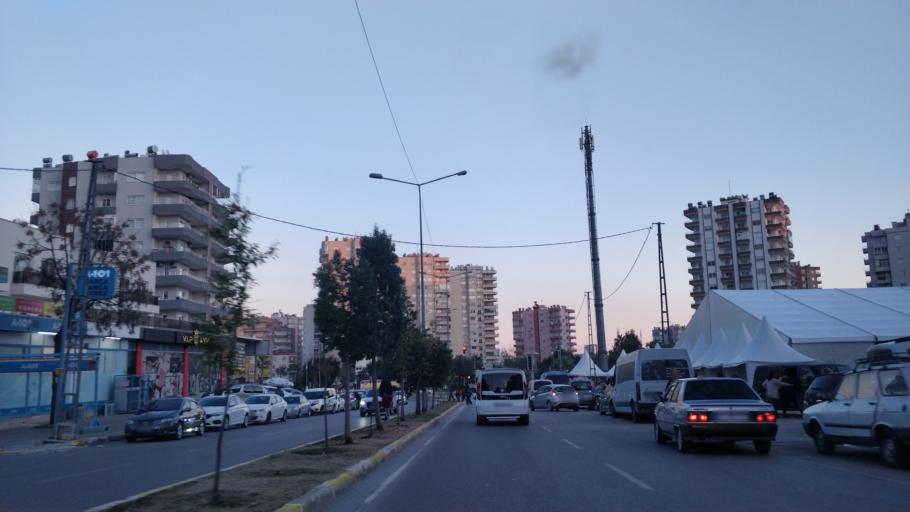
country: TR
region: Mersin
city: Mercin
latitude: 36.7912
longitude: 34.5903
